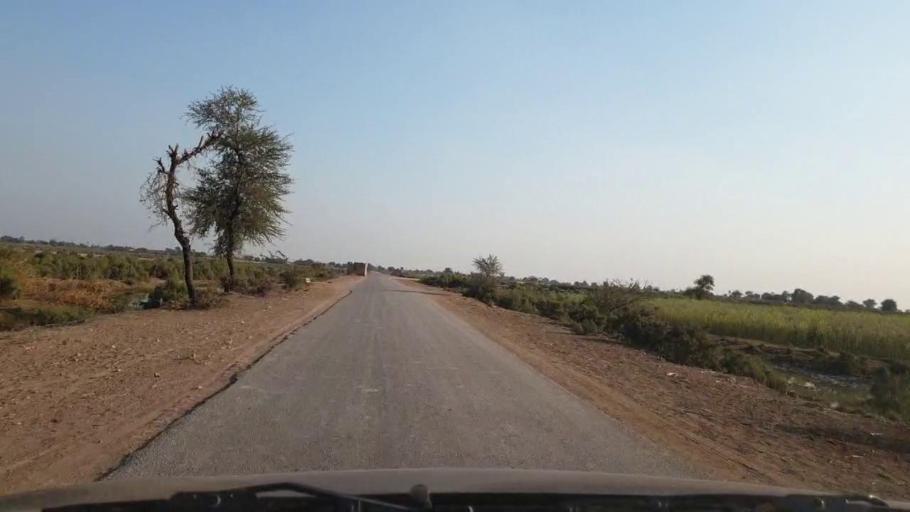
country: PK
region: Sindh
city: Jhol
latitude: 25.9371
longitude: 68.9131
